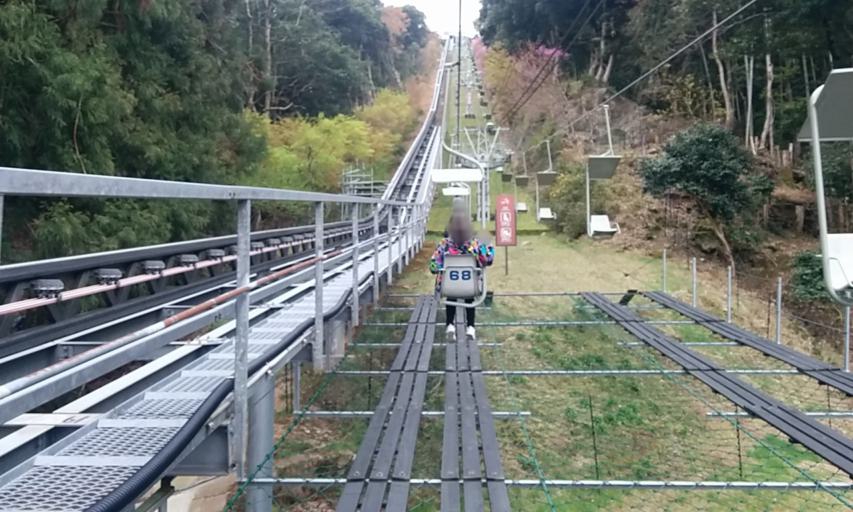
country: JP
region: Kyoto
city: Miyazu
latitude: 35.5634
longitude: 135.1985
